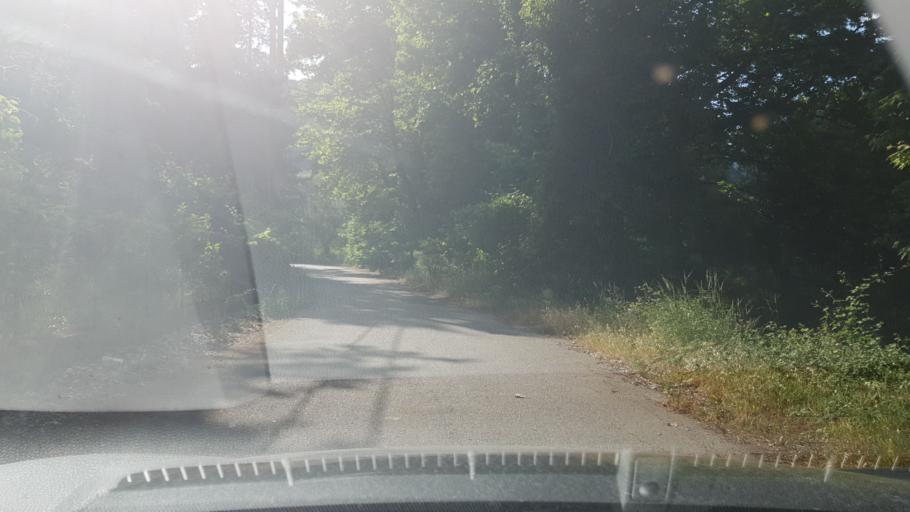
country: GR
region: Ionian Islands
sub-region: Lefkada
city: Nidri
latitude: 38.7155
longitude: 20.6999
